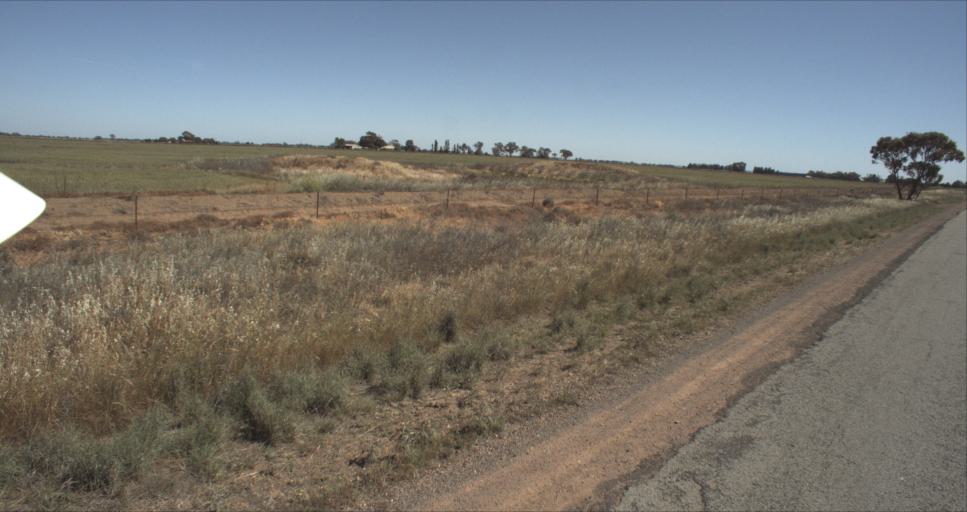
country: AU
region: New South Wales
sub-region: Leeton
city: Leeton
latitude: -34.5554
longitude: 146.3138
